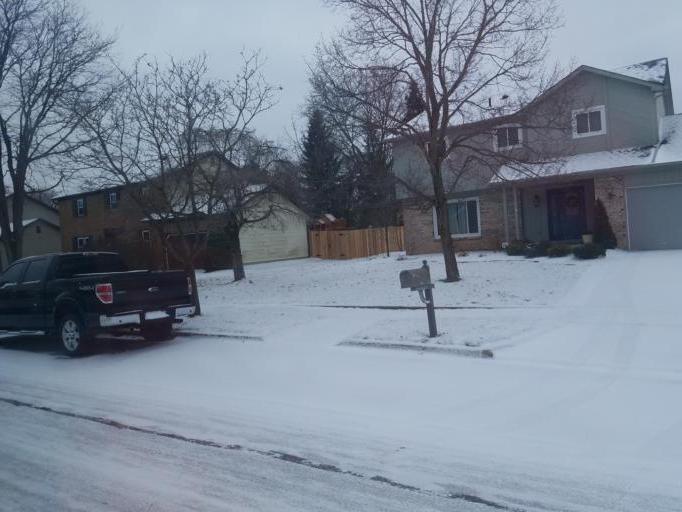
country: US
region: Ohio
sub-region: Delaware County
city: Powell
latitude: 40.1263
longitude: -83.0723
